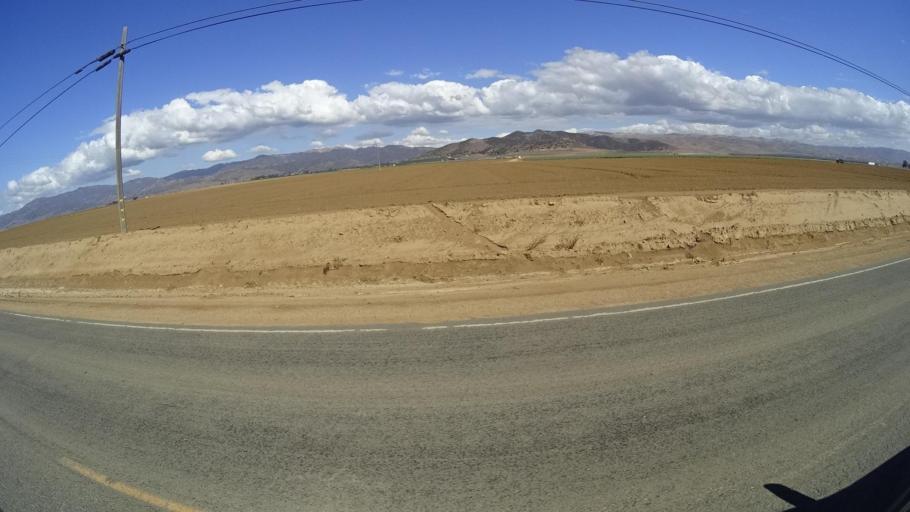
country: US
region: California
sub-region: Monterey County
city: Chualar
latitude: 36.5611
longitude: -121.4834
